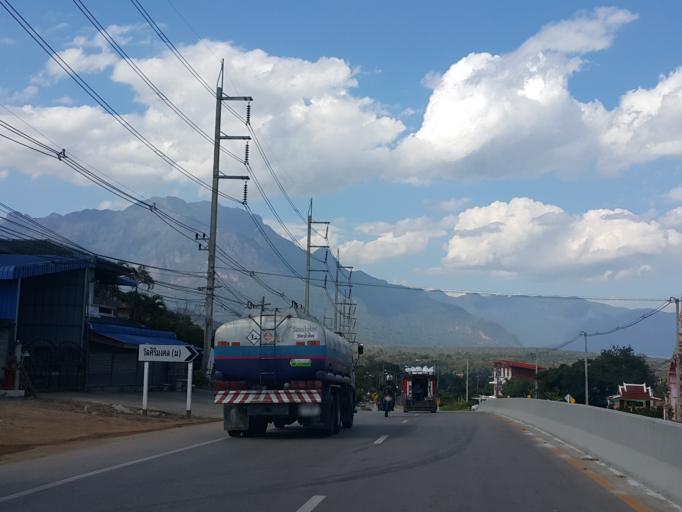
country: TH
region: Chiang Mai
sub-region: Amphoe Chiang Dao
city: Chiang Dao
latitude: 19.3197
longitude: 98.9557
